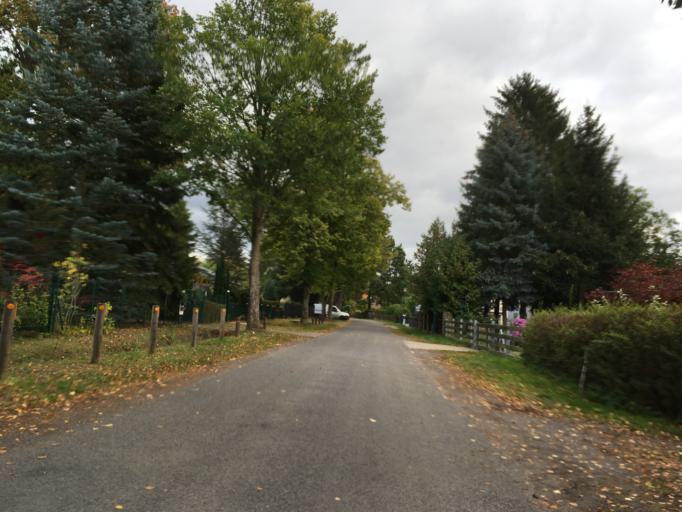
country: DE
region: Brandenburg
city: Birkenwerder
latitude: 52.6875
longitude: 13.3148
